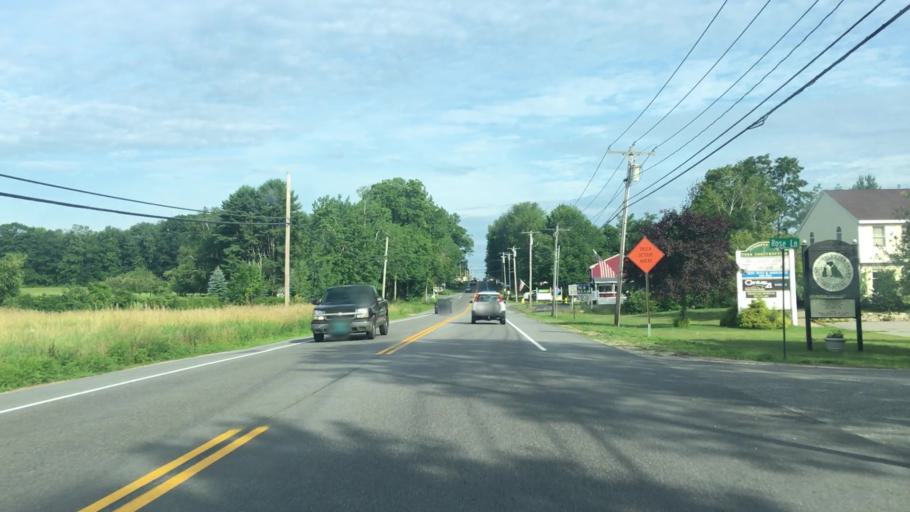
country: US
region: Maine
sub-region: York County
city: Buxton
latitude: 43.7326
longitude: -70.5451
